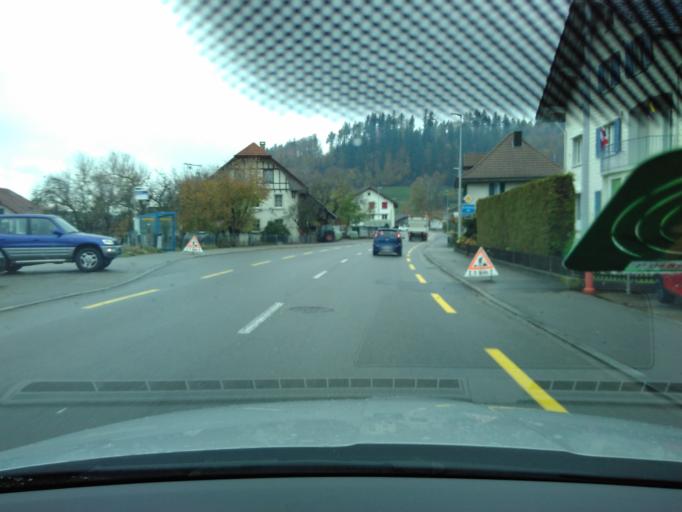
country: CH
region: Aargau
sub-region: Bezirk Zofingen
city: Kirchleerau
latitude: 47.2715
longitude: 8.0647
